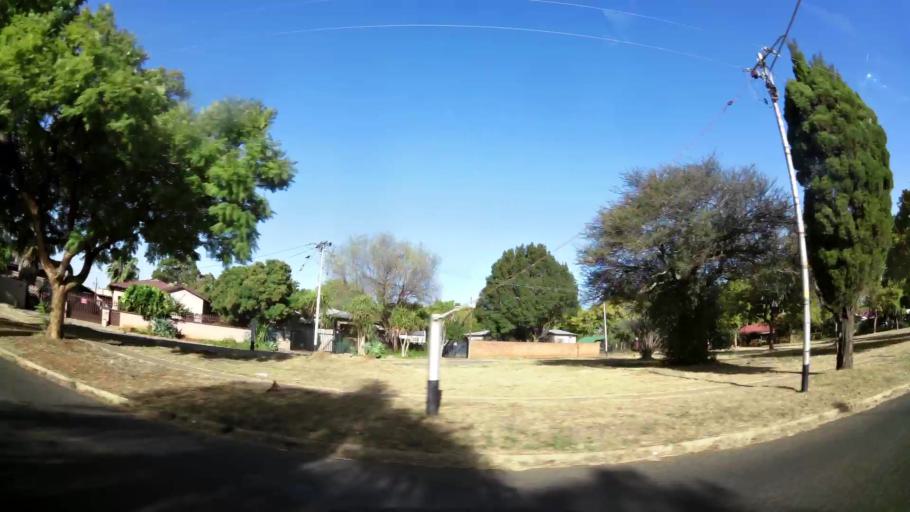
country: ZA
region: Gauteng
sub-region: City of Tshwane Metropolitan Municipality
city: Pretoria
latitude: -25.7075
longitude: 28.2283
